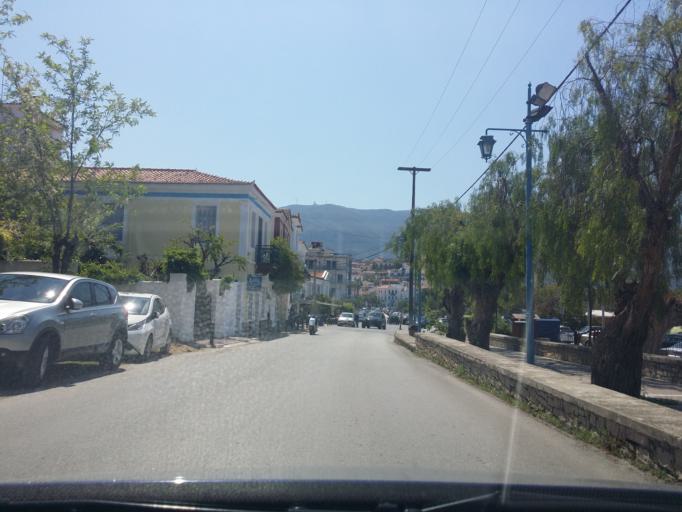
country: GR
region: Attica
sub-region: Nomos Piraios
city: Poros
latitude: 37.5029
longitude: 23.4553
